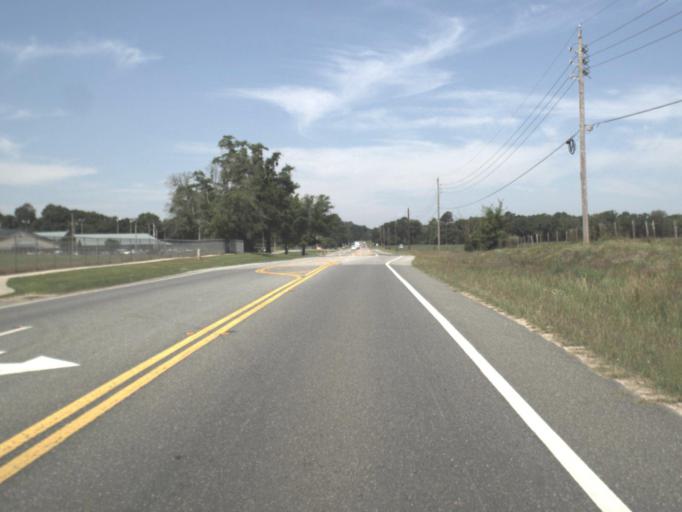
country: US
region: Florida
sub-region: Jackson County
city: Marianna
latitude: 30.8124
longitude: -85.1961
